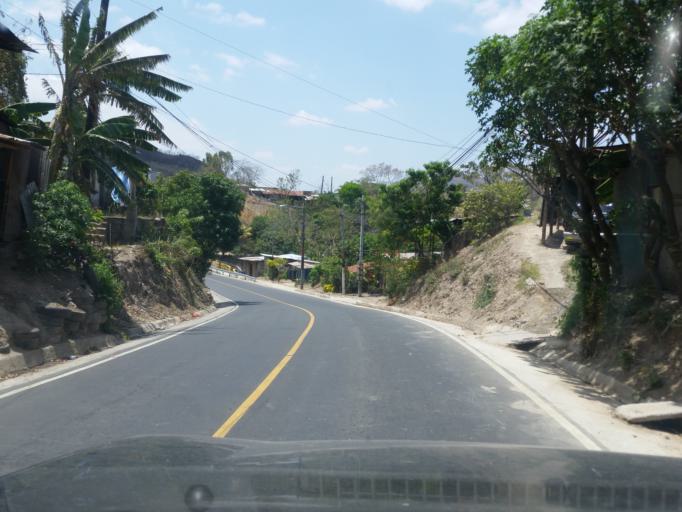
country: NI
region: Boaco
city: Boaco
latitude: 12.4708
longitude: -85.6503
